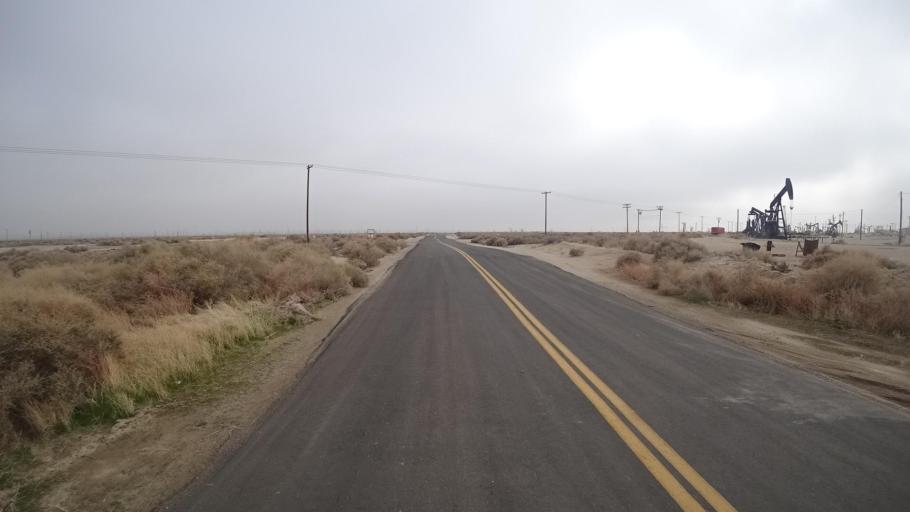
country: US
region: California
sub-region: Kern County
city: Maricopa
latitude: 35.0818
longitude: -119.3845
